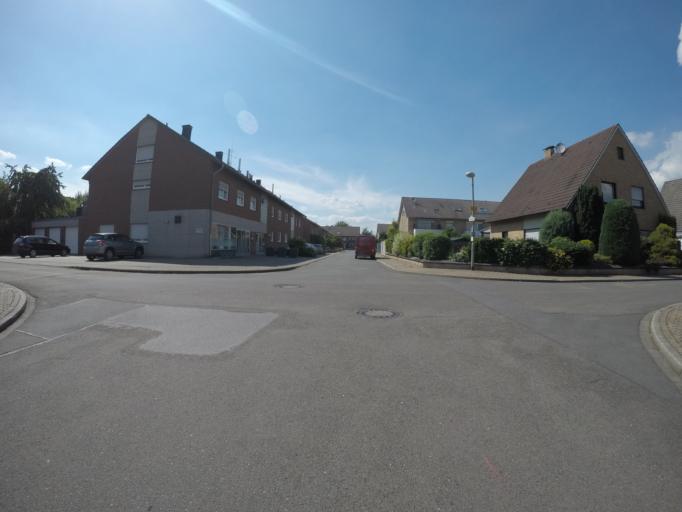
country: DE
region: North Rhine-Westphalia
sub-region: Regierungsbezirk Munster
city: Isselburg
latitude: 51.8503
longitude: 6.4268
